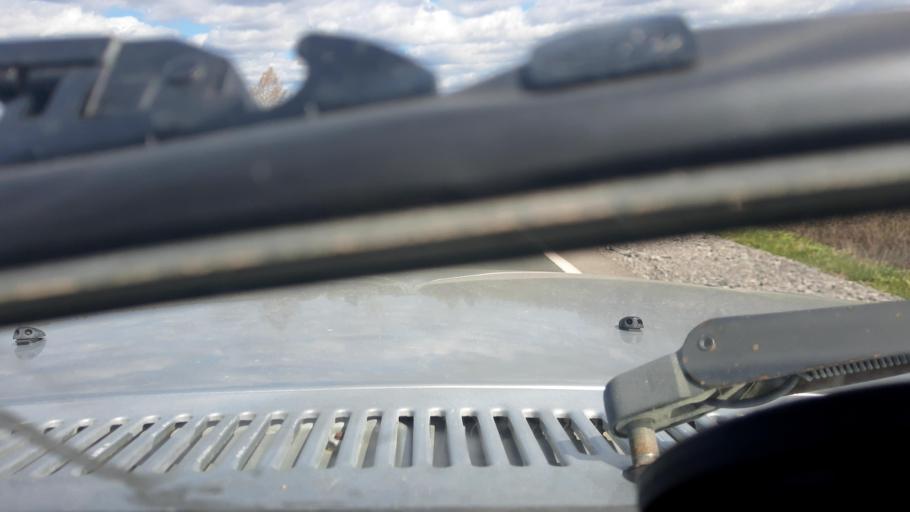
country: RU
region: Bashkortostan
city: Yazykovo
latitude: 55.2973
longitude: 56.3006
